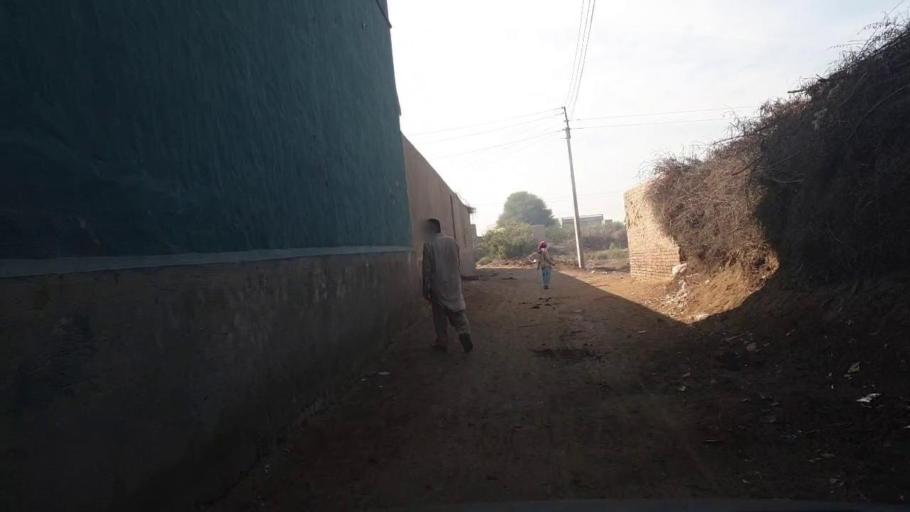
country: PK
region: Sindh
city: Shahpur Chakar
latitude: 26.1728
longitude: 68.5840
